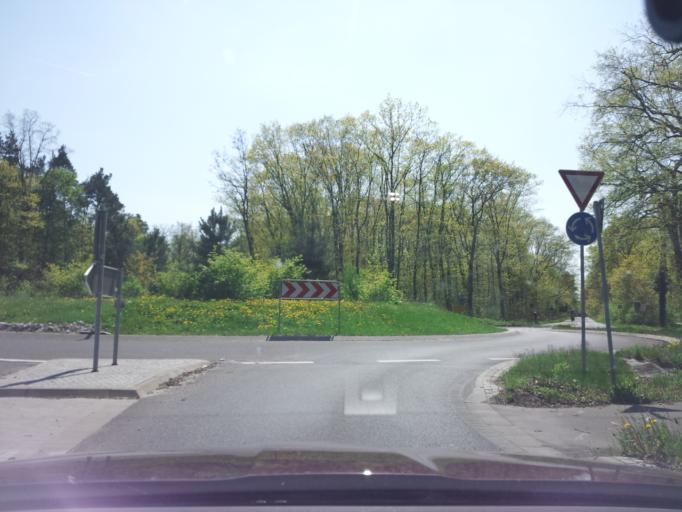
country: DE
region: Brandenburg
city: Stahnsdorf
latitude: 52.3602
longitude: 13.1895
